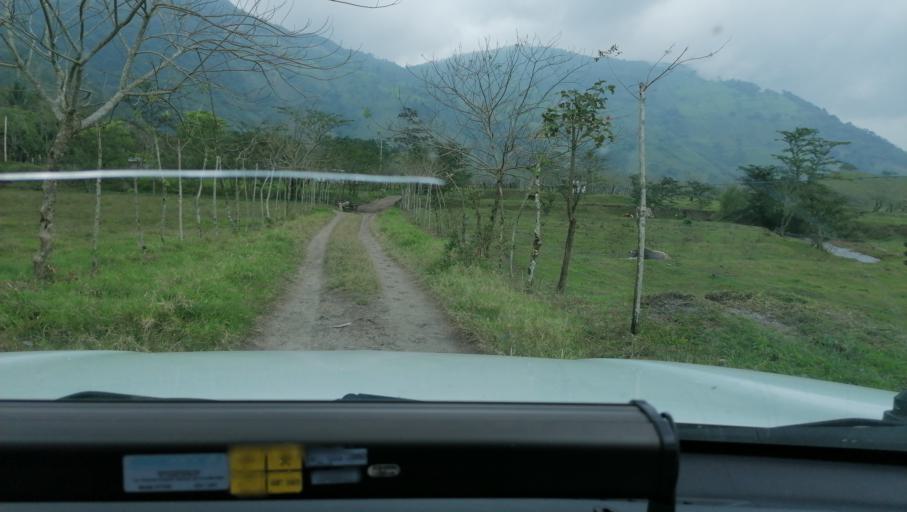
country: MX
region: Chiapas
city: Ixtacomitan
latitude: 17.3663
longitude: -93.1840
